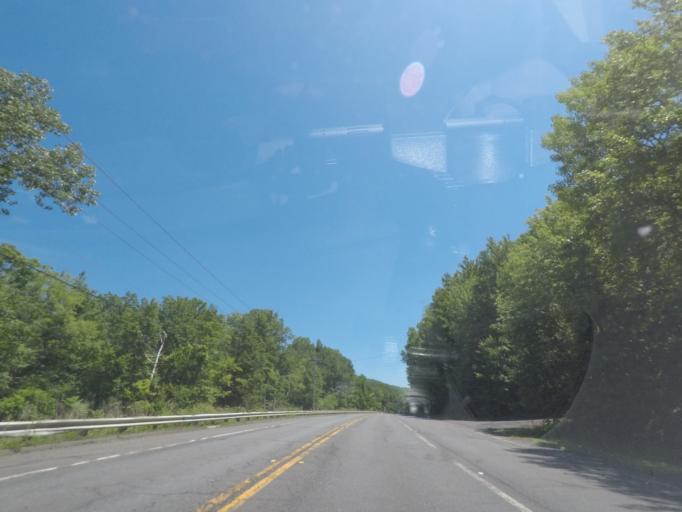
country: US
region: Massachusetts
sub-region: Hampden County
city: Westfield
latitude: 42.1783
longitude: -72.8368
